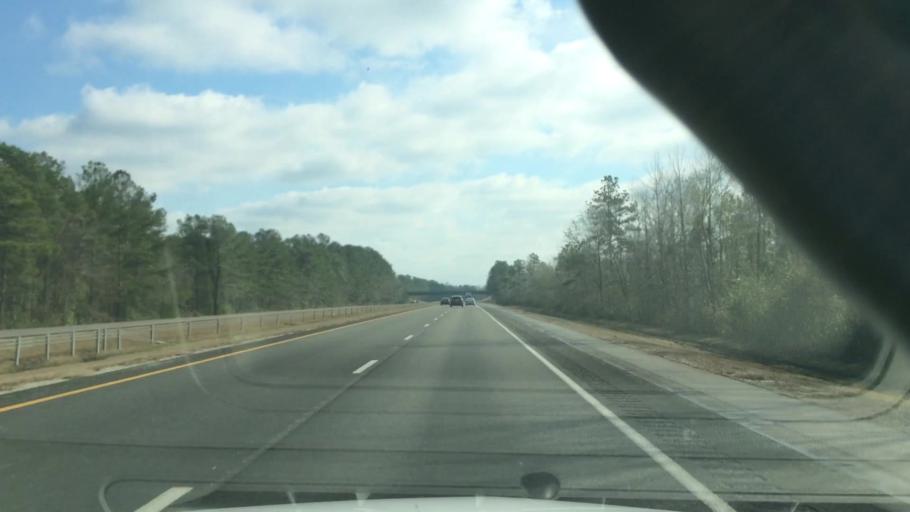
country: US
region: North Carolina
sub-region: Pender County
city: Burgaw
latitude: 34.6161
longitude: -77.9248
